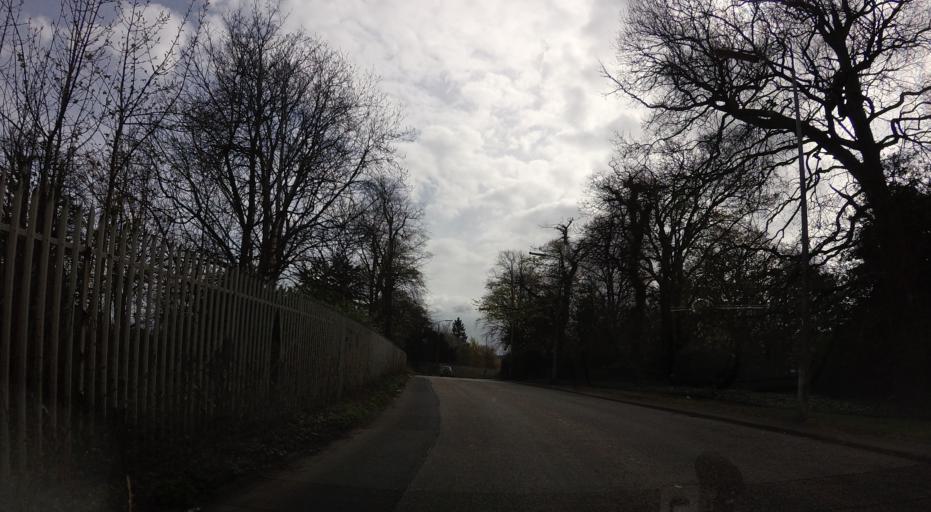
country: GB
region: Scotland
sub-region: Edinburgh
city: Edinburgh
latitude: 55.9790
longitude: -3.2548
